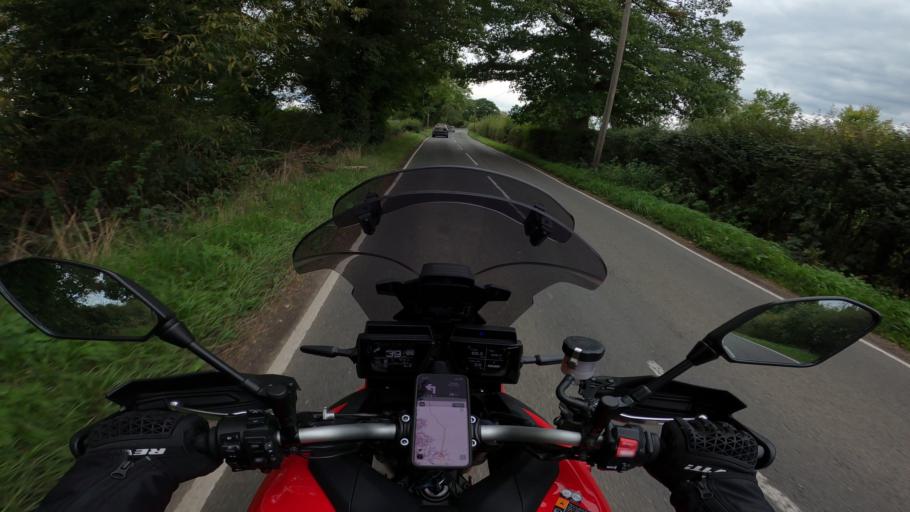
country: GB
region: England
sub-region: Surrey
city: Lingfield
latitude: 51.1886
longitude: 0.0011
